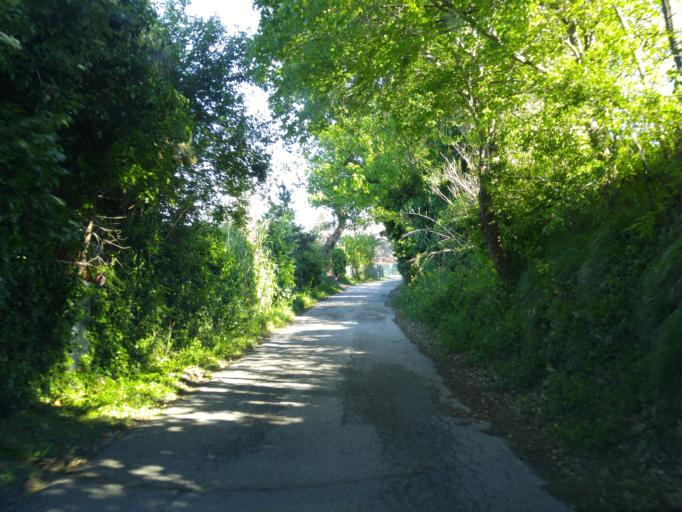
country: IT
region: The Marches
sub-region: Provincia di Pesaro e Urbino
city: Monteciccardo
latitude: 43.8263
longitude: 12.8327
